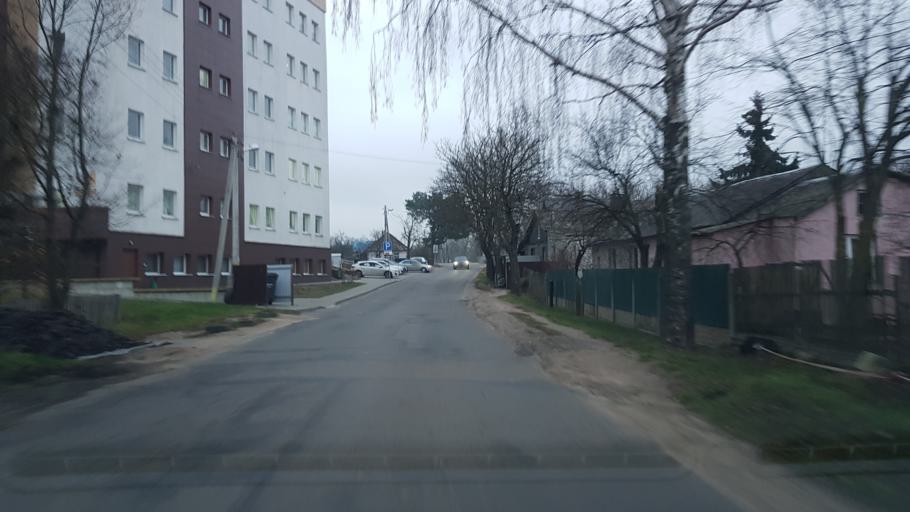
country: BY
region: Minsk
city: Minsk
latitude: 53.9385
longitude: 27.5377
